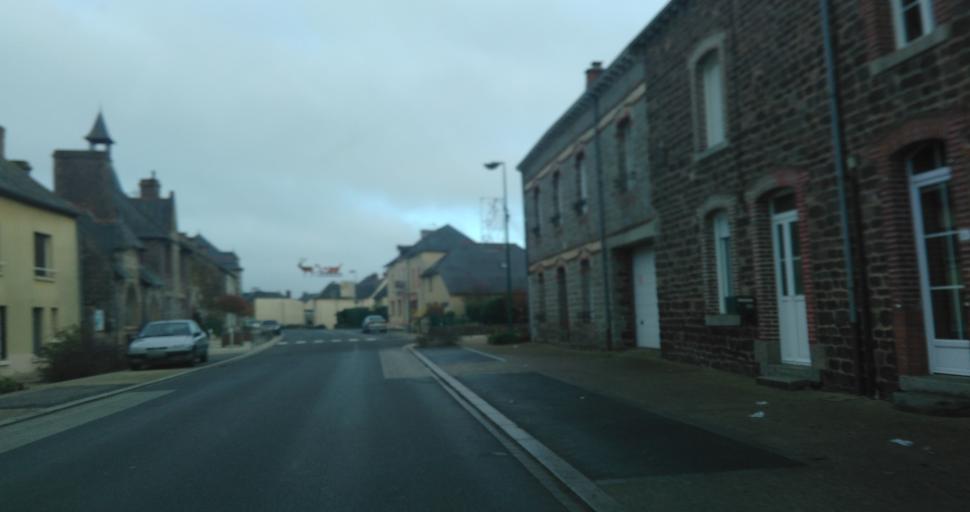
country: FR
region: Brittany
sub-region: Departement d'Ille-et-Vilaine
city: Boisgervilly
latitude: 48.1665
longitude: -2.0676
